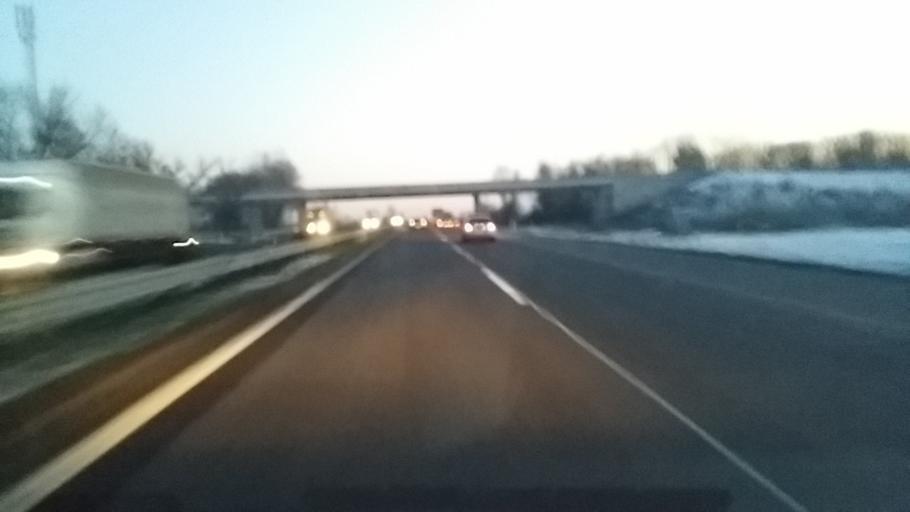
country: AT
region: Lower Austria
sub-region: Politischer Bezirk Mistelbach
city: Rabensburg
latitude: 48.6135
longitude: 17.0132
